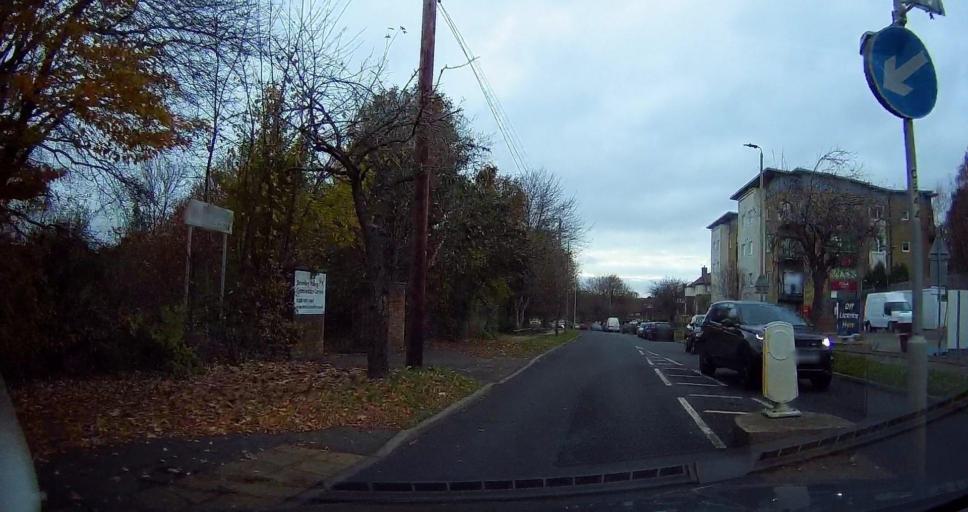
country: GB
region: England
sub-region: Greater London
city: Sidcup
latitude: 51.4055
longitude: 0.1043
